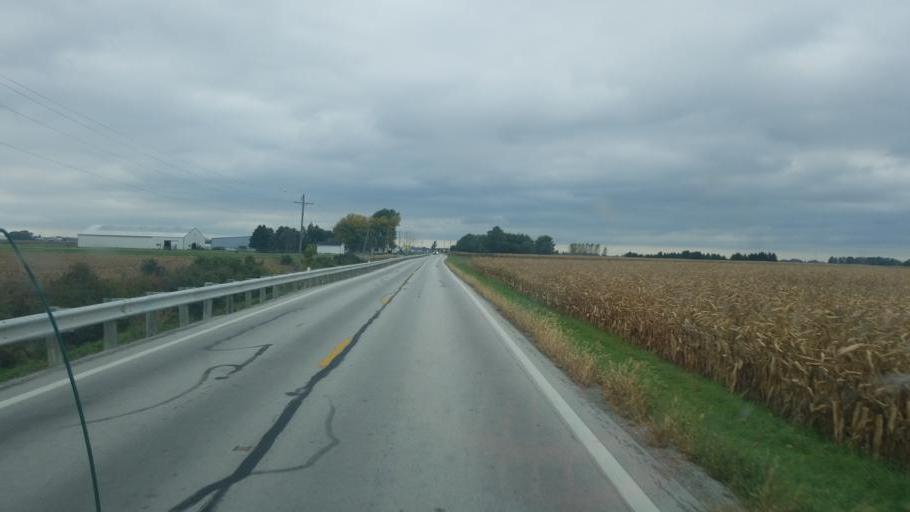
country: US
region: Ohio
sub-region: Wood County
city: Haskins
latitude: 41.4435
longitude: -83.6973
